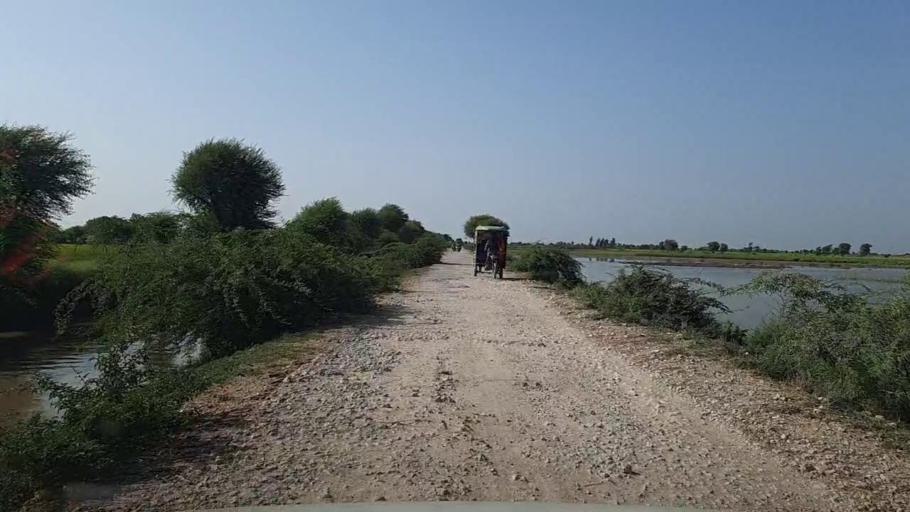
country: PK
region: Sindh
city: Kario
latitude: 24.7975
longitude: 68.5567
